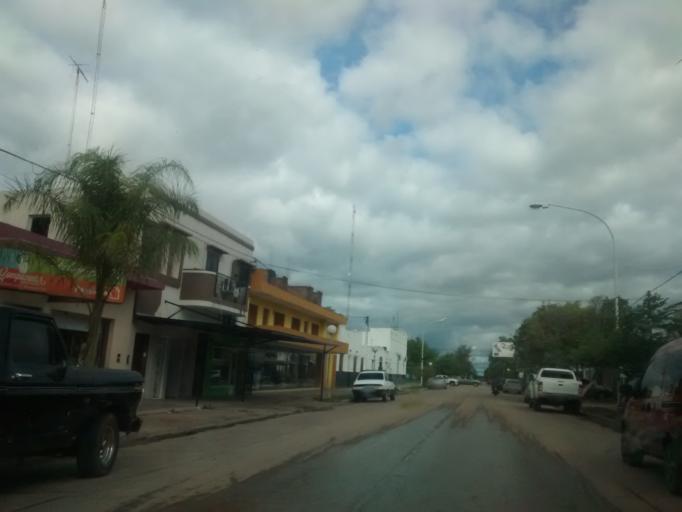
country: AR
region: Chaco
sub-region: Departamento de Quitilipi
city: Quitilipi
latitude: -26.8708
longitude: -60.2171
